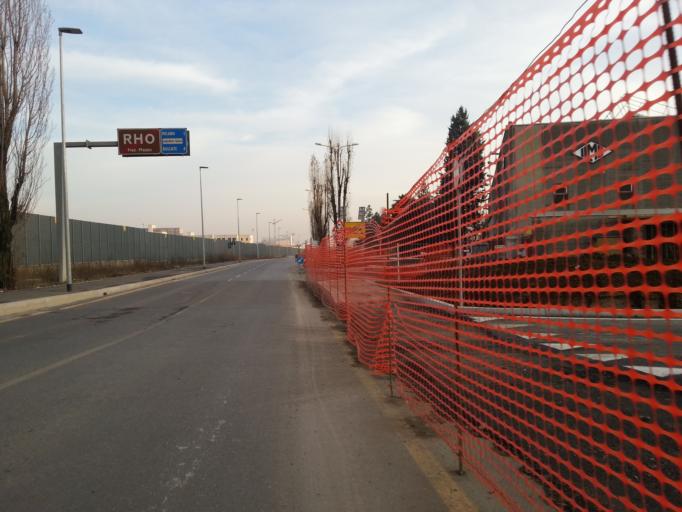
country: IT
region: Lombardy
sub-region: Citta metropolitana di Milano
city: Pero
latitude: 45.5253
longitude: 9.0939
